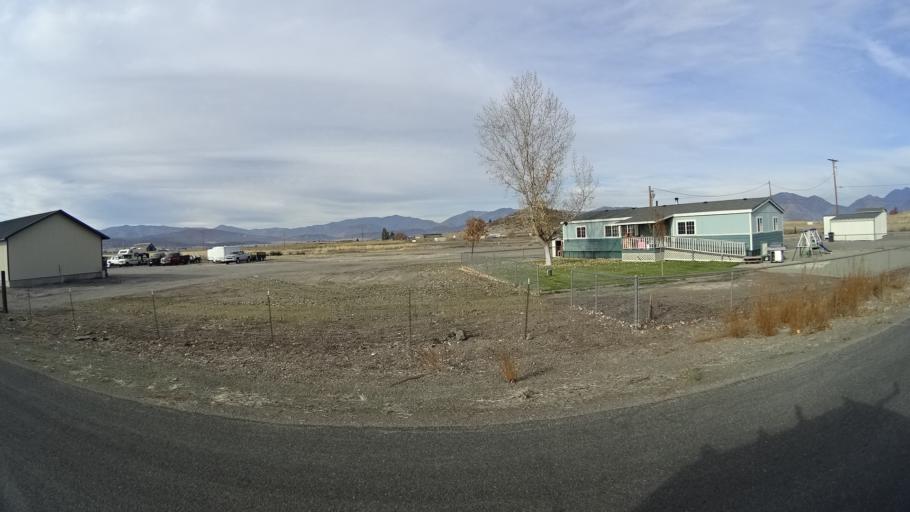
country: US
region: California
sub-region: Siskiyou County
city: Montague
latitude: 41.7256
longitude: -122.5406
